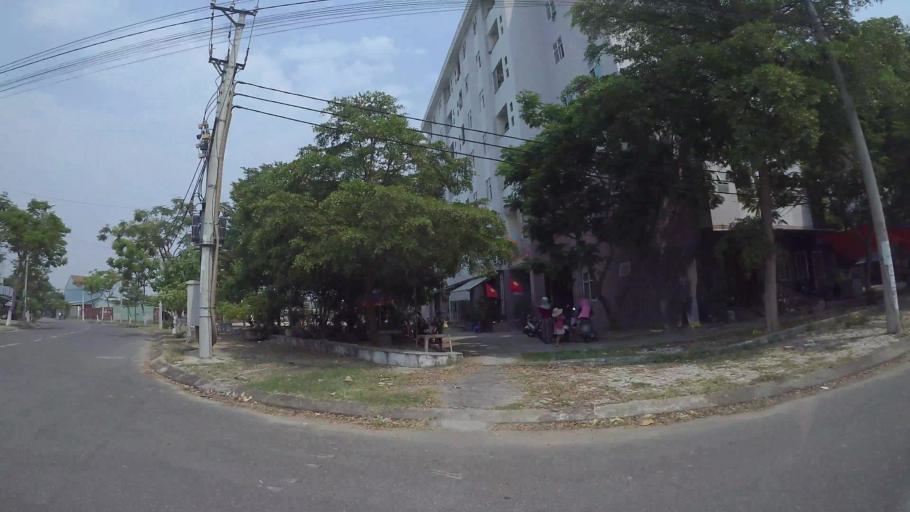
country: VN
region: Da Nang
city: Cam Le
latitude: 16.0002
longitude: 108.2046
